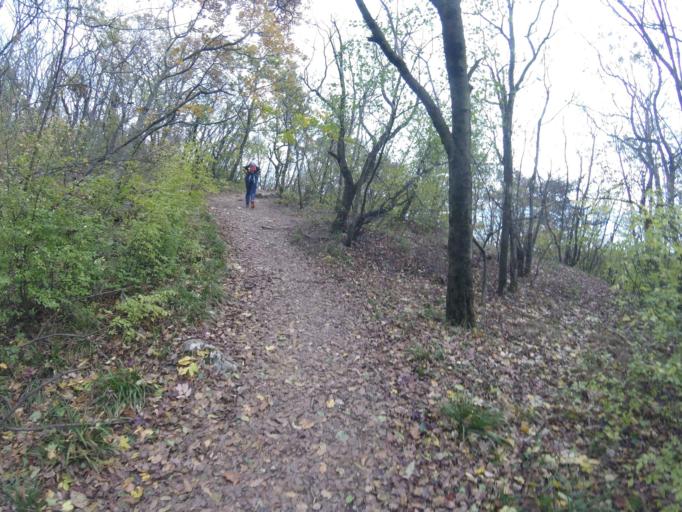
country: HU
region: Pest
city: Budakeszi
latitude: 47.5299
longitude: 18.9657
